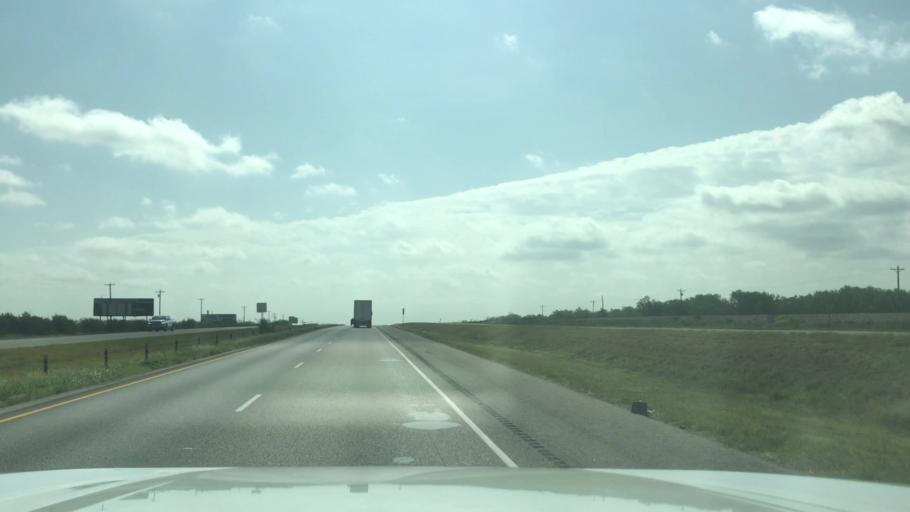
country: US
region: Texas
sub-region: Taylor County
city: Merkel
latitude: 32.4648
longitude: -99.9682
